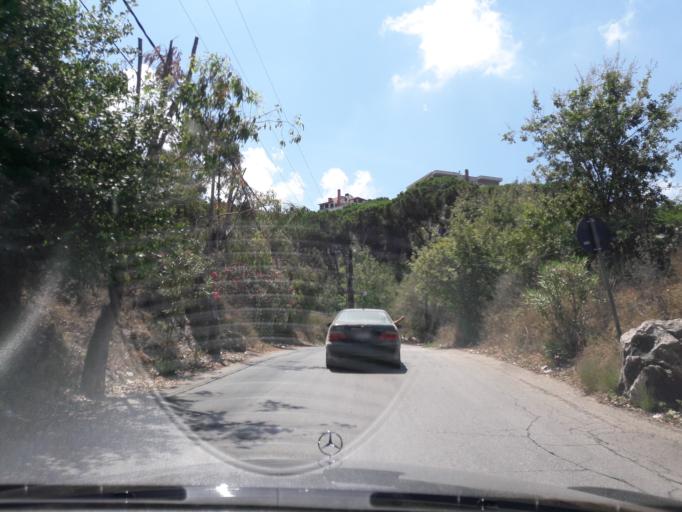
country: LB
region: Mont-Liban
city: Djounie
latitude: 33.9256
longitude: 35.6606
